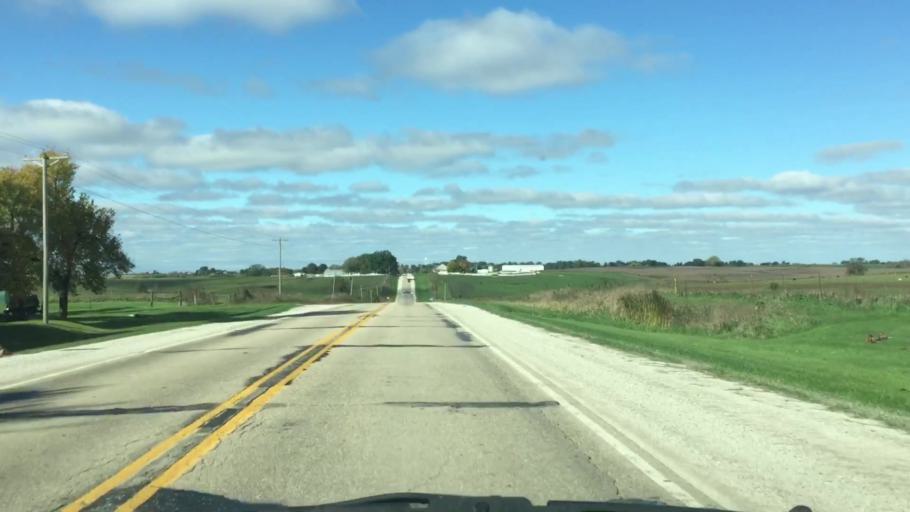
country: US
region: Iowa
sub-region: Decatur County
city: Leon
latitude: 40.7420
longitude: -93.8046
